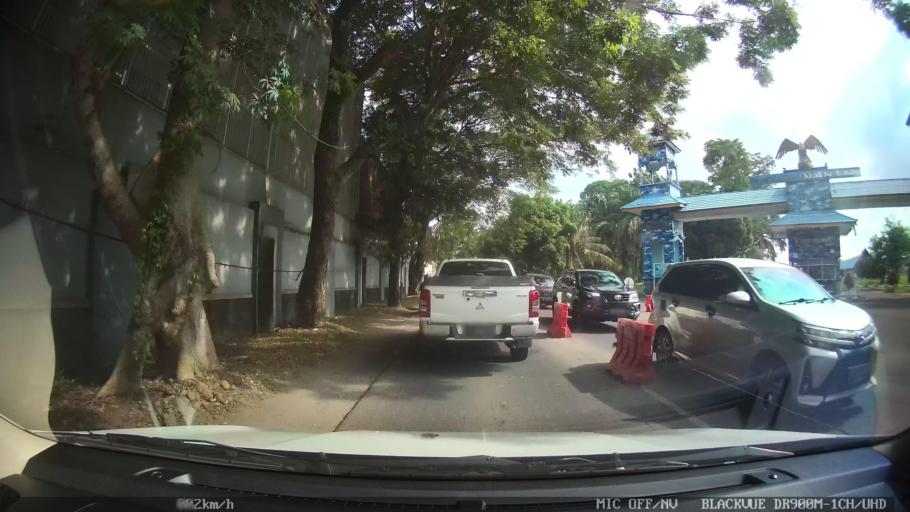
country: ID
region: North Sumatra
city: Medan
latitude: 3.5639
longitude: 98.6836
